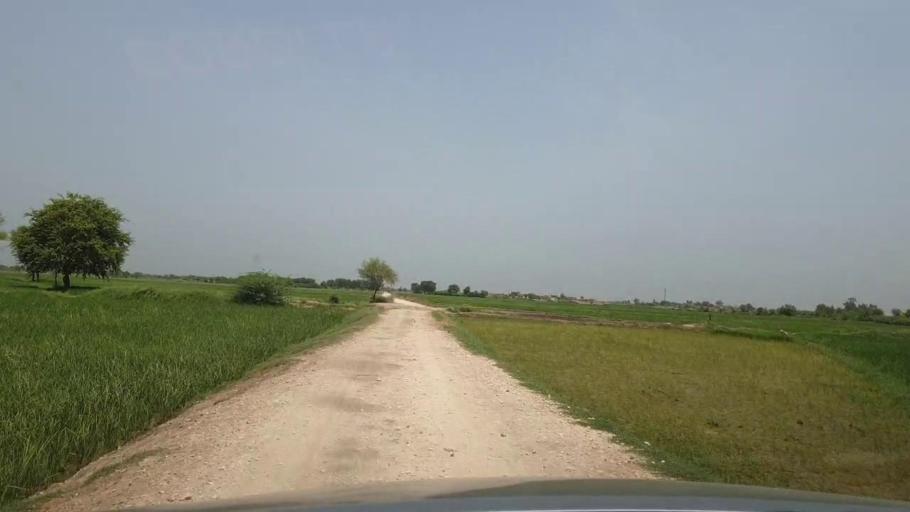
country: PK
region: Sindh
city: Madeji
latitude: 27.7546
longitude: 68.3713
